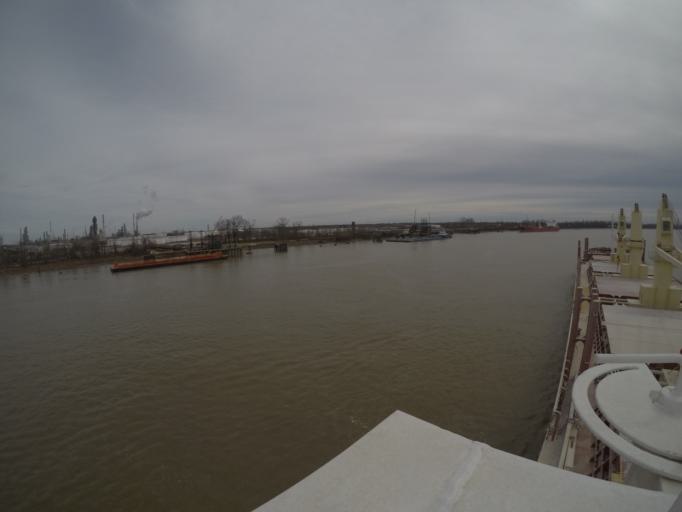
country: US
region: Louisiana
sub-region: Saint Charles Parish
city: Hahnville
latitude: 29.9878
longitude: -90.4034
